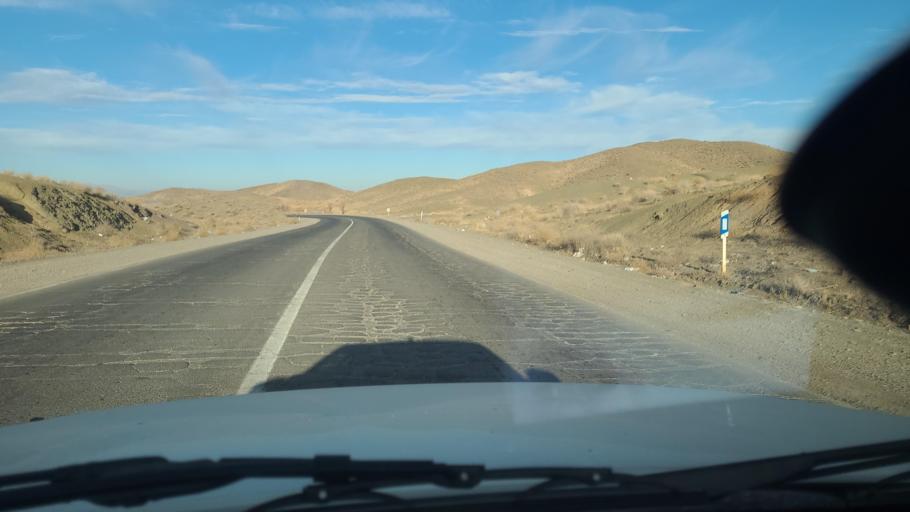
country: IR
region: Razavi Khorasan
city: Sabzevar
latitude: 36.4104
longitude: 57.5495
